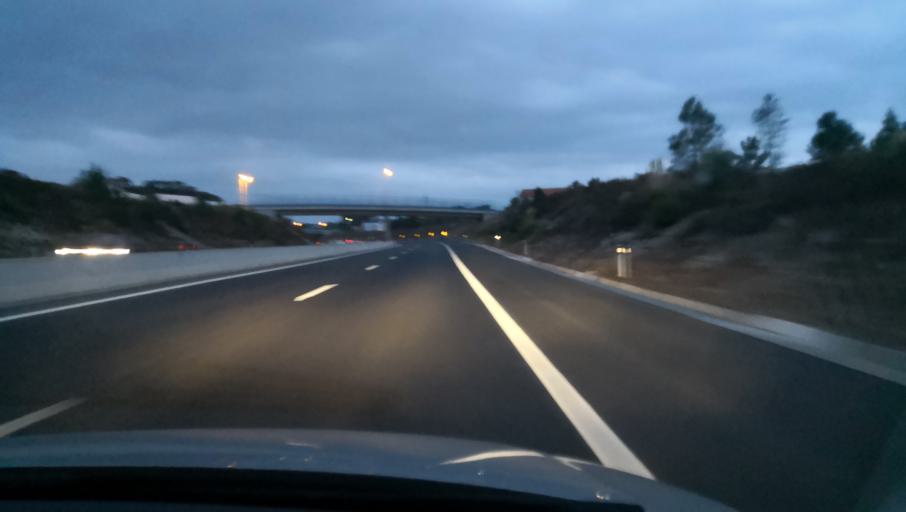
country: PT
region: Setubal
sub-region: Seixal
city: Arrentela
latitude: 38.5956
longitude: -9.1008
